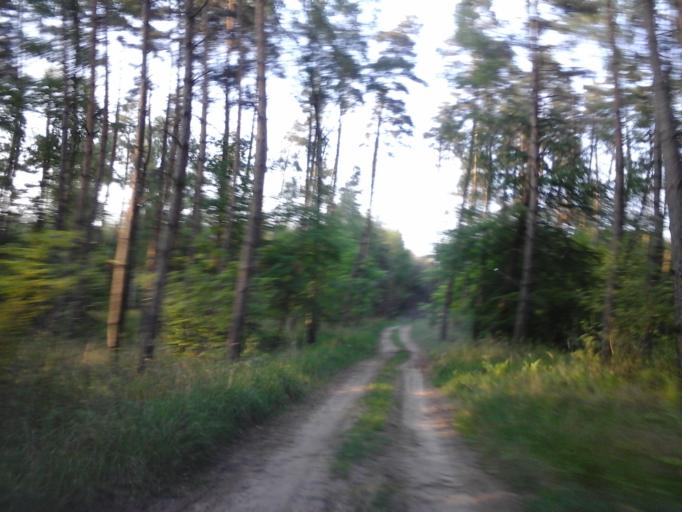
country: PL
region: West Pomeranian Voivodeship
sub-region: Powiat choszczenski
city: Krzecin
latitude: 53.0163
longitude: 15.5496
